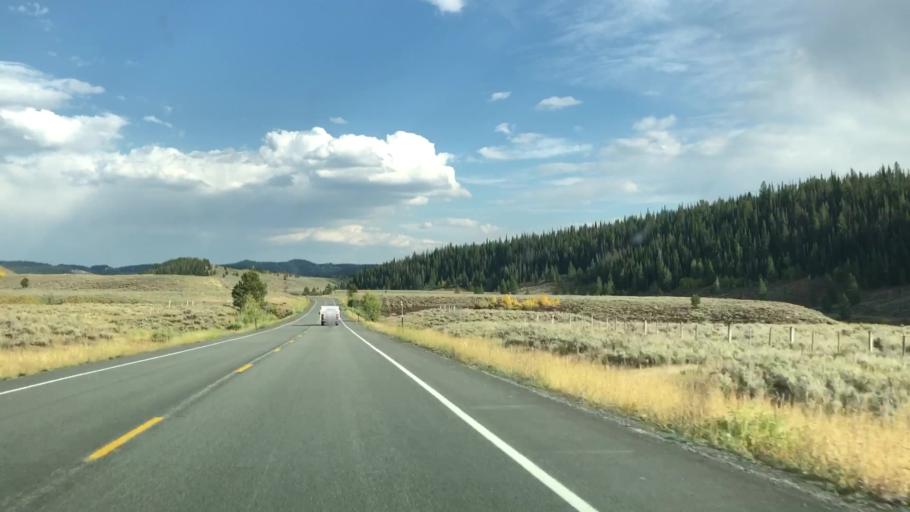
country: US
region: Wyoming
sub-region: Teton County
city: Hoback
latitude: 43.1540
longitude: -110.2961
